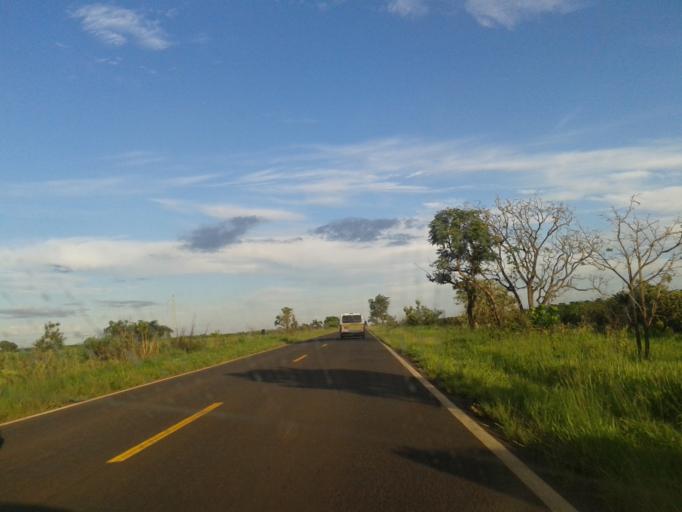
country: BR
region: Minas Gerais
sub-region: Araguari
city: Araguari
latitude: -18.6283
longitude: -48.2346
